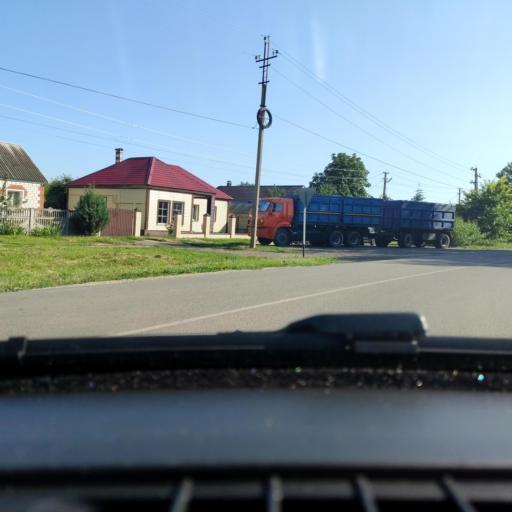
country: RU
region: Voronezj
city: Panino
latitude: 51.6470
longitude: 40.1433
